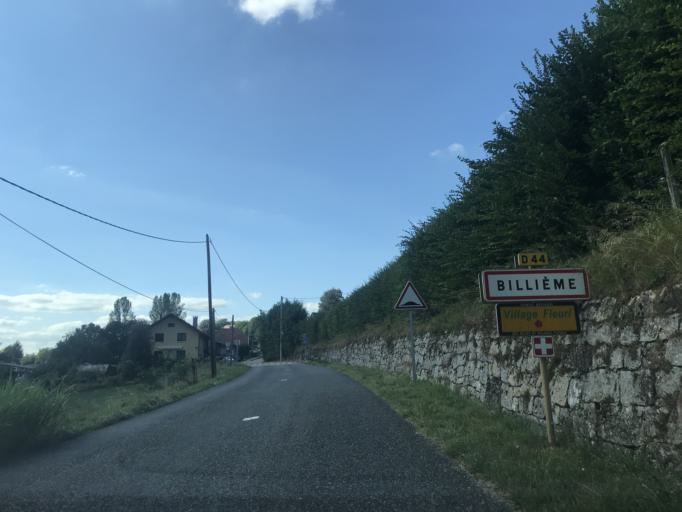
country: FR
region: Rhone-Alpes
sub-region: Departement de la Savoie
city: Yenne
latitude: 45.7173
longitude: 5.8122
